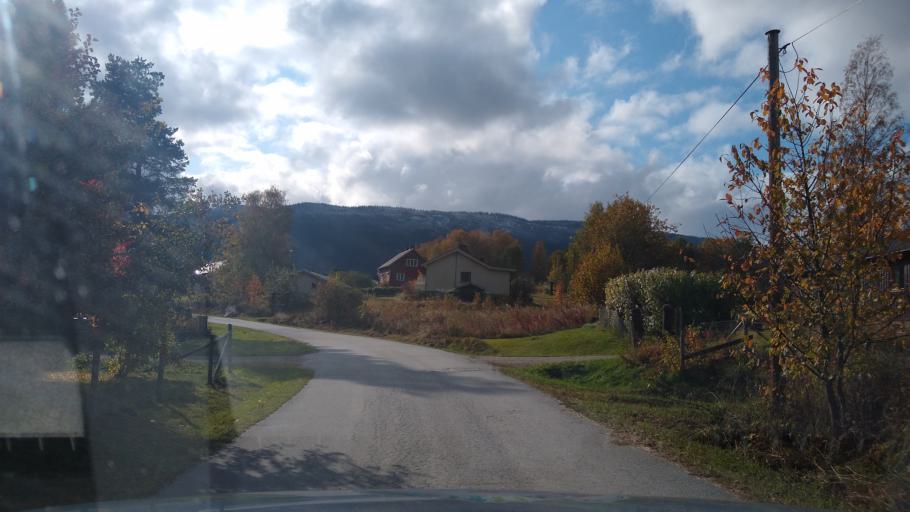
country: NO
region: Oppland
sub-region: Ringebu
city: Ringebu
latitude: 61.5406
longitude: 10.1334
